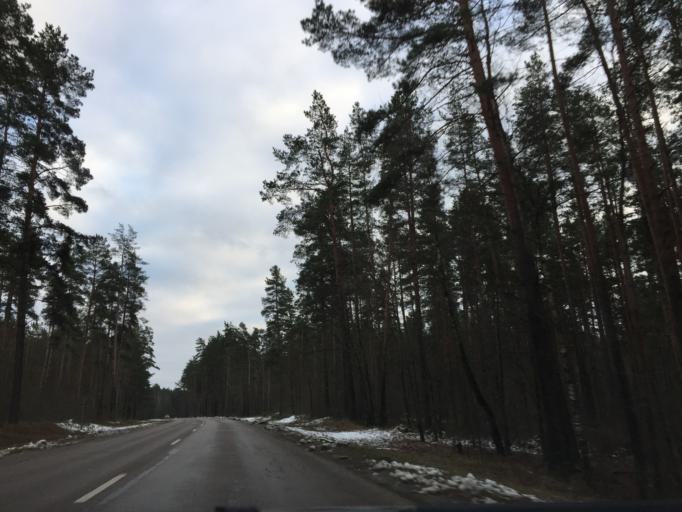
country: LV
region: Stopini
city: Ulbroka
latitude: 56.9601
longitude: 24.3048
